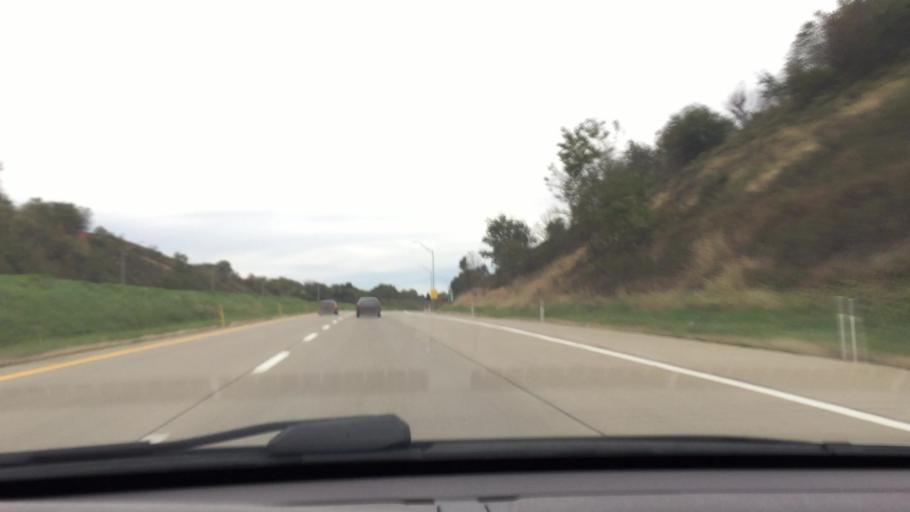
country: US
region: Pennsylvania
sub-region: Lawrence County
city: Oakland
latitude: 40.9633
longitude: -80.3985
